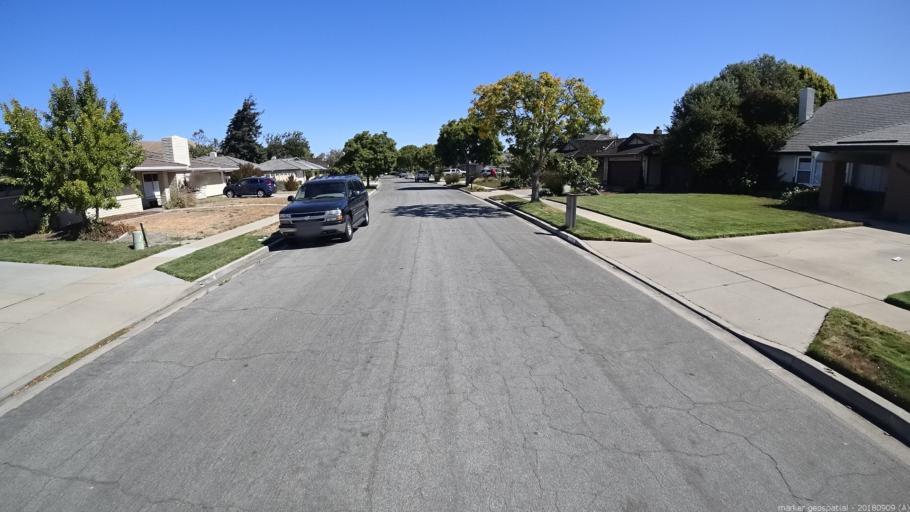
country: US
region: California
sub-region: Monterey County
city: Salinas
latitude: 36.5980
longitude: -121.7043
